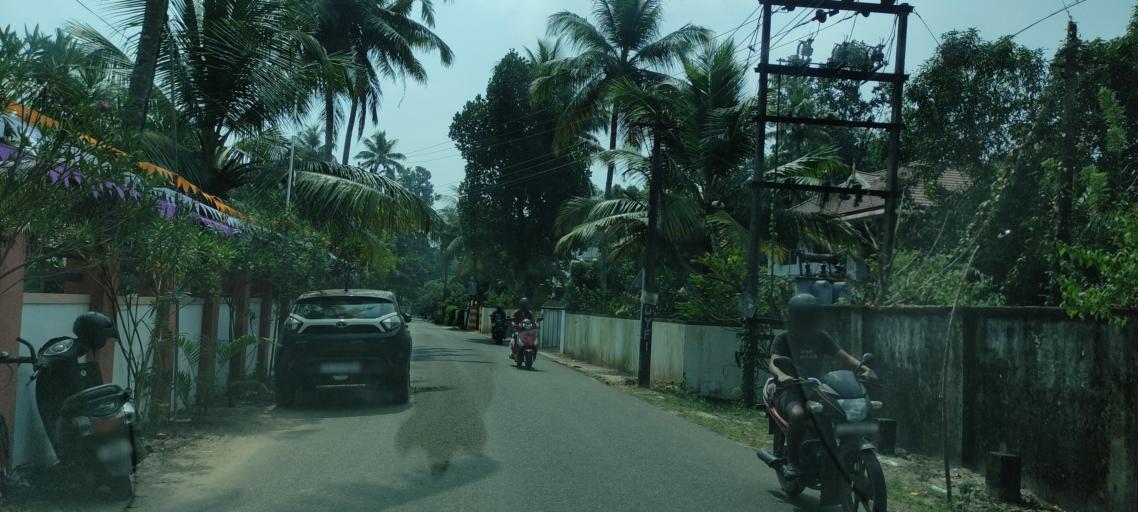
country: IN
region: Kerala
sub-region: Alappuzha
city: Shertallai
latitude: 9.6524
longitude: 76.3571
